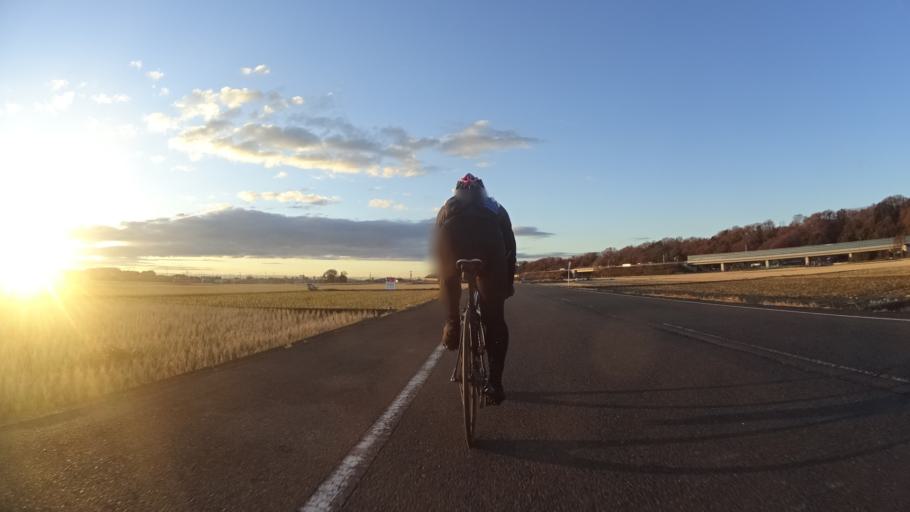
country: JP
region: Kanagawa
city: Zama
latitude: 35.5106
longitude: 139.3677
